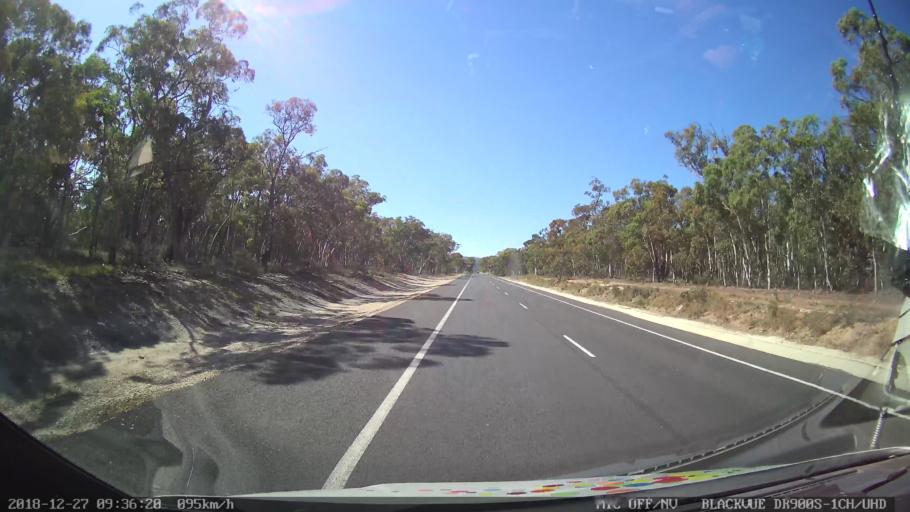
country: AU
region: New South Wales
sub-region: Lithgow
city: Portland
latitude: -33.2509
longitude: 150.0345
